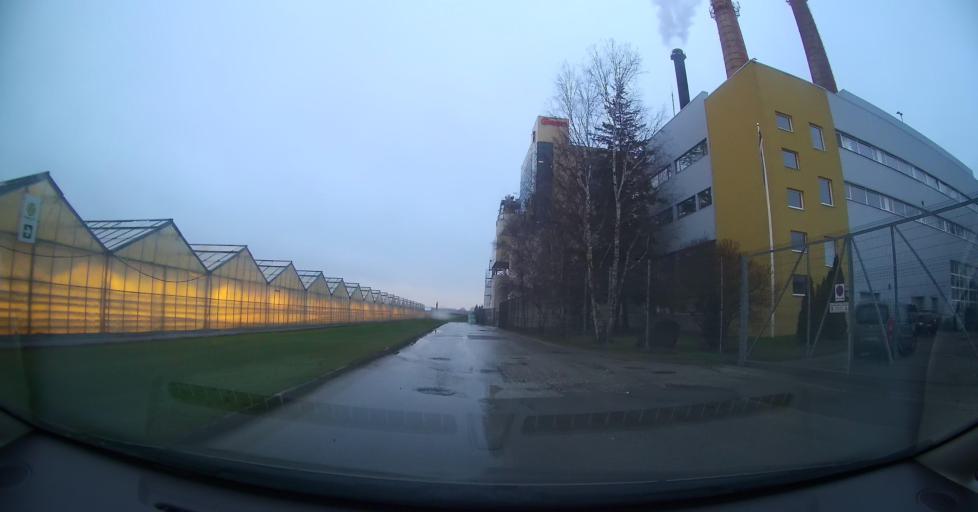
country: EE
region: Tartu
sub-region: Tartu linn
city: Tartu
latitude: 58.3693
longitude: 26.7926
